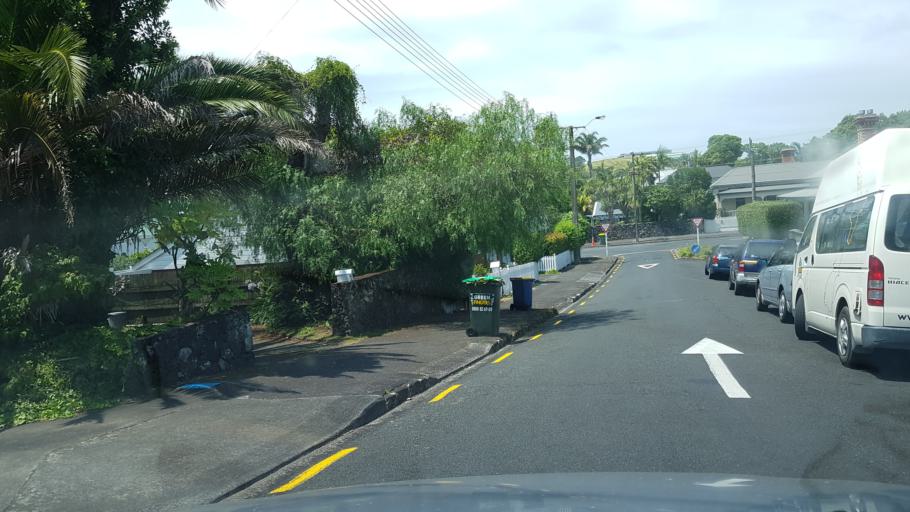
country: NZ
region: Auckland
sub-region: Auckland
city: Auckland
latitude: -36.8261
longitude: 174.8023
